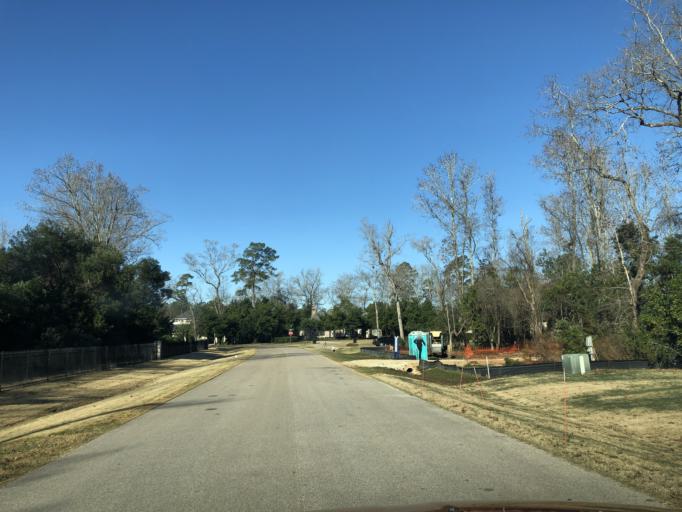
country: US
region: Texas
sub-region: Montgomery County
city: Porter Heights
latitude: 30.0713
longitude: -95.3339
